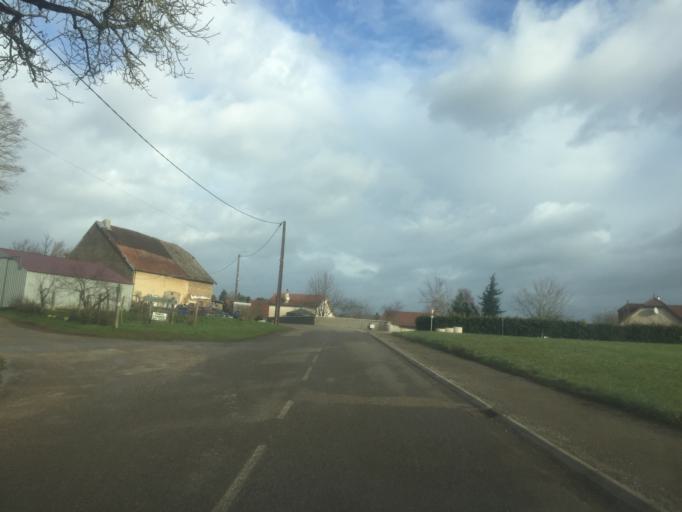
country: FR
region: Franche-Comte
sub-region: Departement du Jura
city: Orchamps
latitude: 47.2076
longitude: 5.6833
